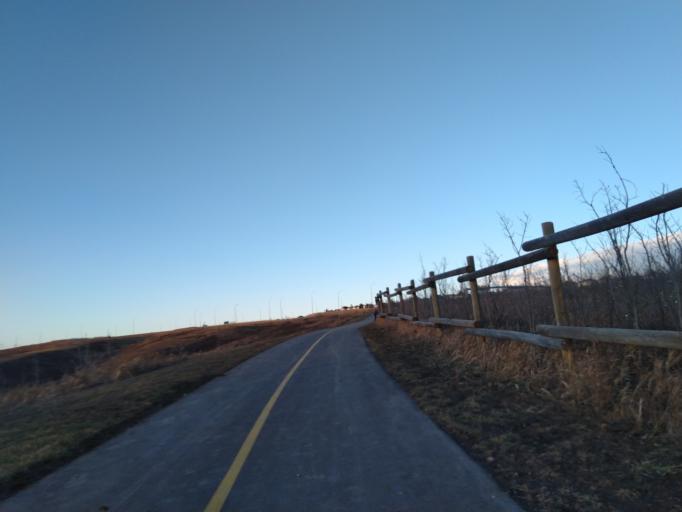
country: CA
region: Alberta
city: Calgary
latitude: 51.1111
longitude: -114.2281
